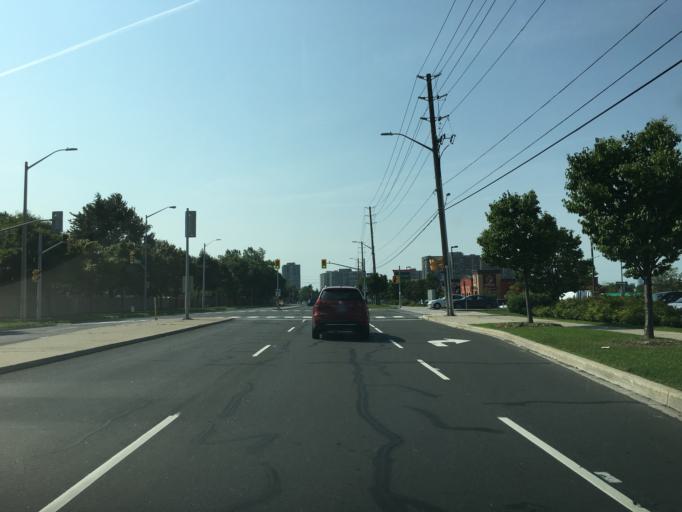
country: CA
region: Ontario
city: Markham
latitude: 43.8227
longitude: -79.3254
